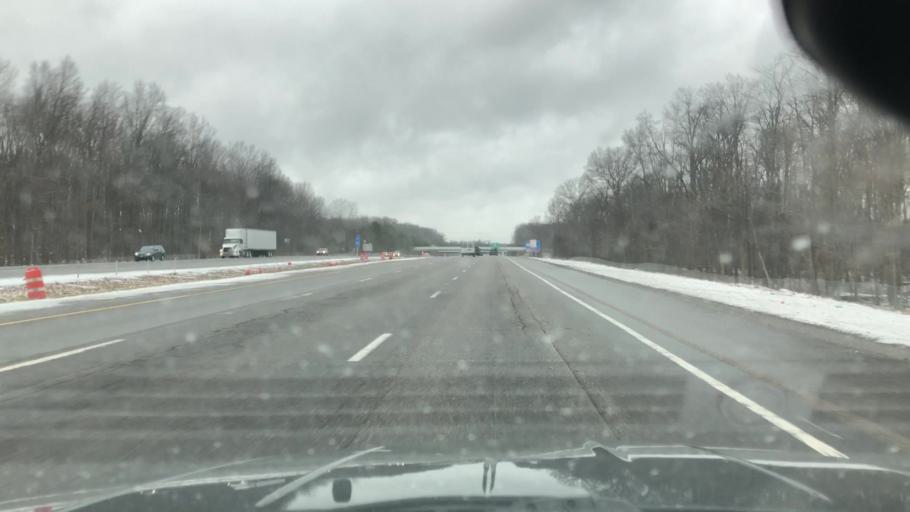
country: US
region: Ohio
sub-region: Cuyahoga County
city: Brecksville
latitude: 41.2957
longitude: -81.6402
